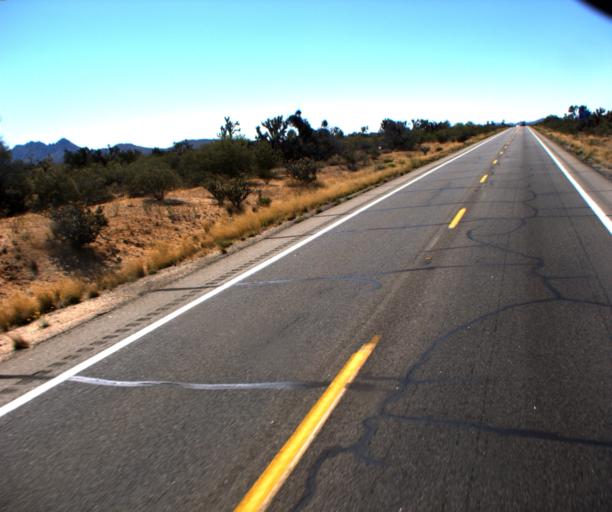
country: US
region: Arizona
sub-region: Yavapai County
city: Congress
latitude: 34.2425
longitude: -113.0773
